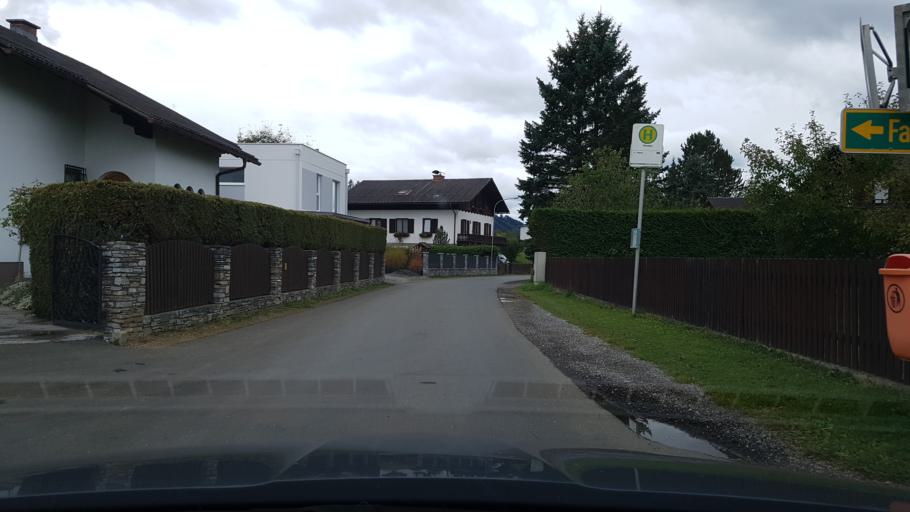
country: AT
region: Styria
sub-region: Politischer Bezirk Bruck-Muerzzuschlag
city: Allerheiligen im Muerztal
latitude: 47.4770
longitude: 15.4058
